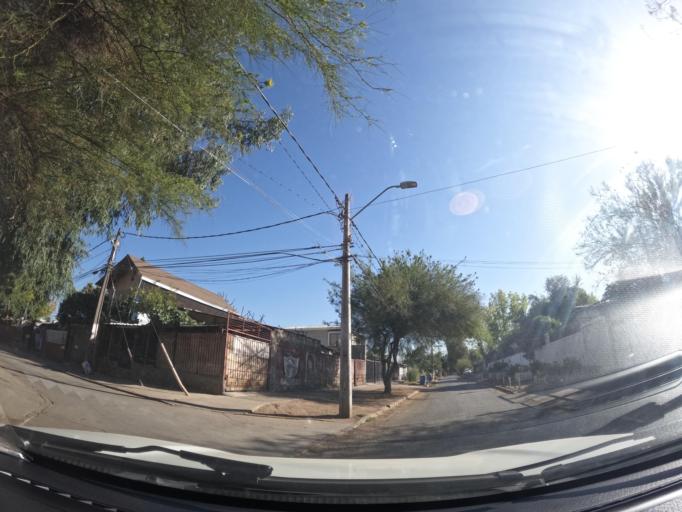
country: CL
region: Santiago Metropolitan
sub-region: Provincia de Santiago
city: Villa Presidente Frei, Nunoa, Santiago, Chile
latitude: -33.4668
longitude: -70.5653
